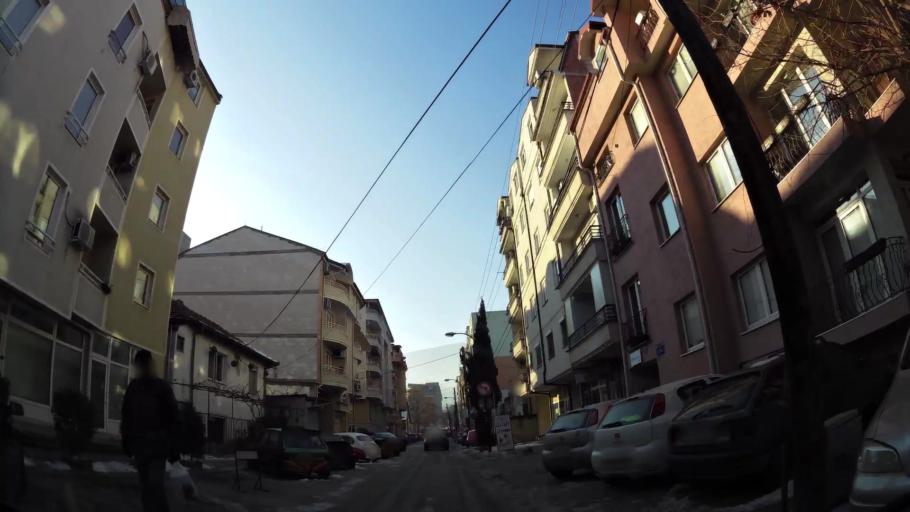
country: MK
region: Karpos
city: Skopje
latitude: 41.9963
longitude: 21.4155
